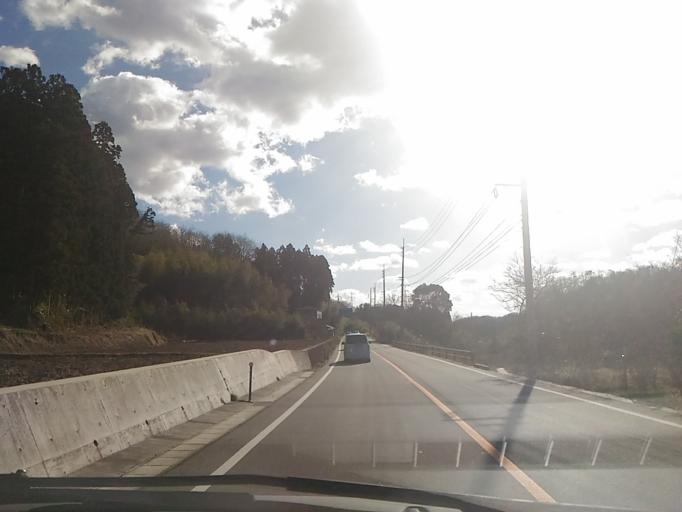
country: JP
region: Fukushima
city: Iwaki
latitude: 37.0054
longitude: 140.7854
